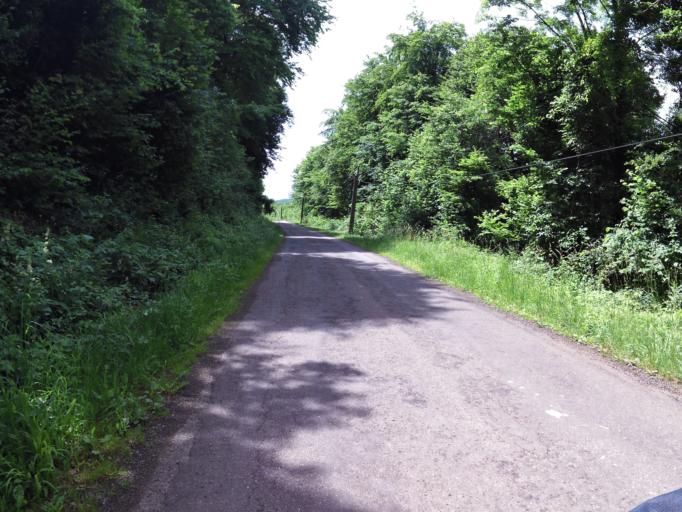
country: FR
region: Lorraine
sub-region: Departement de la Meuse
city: Stenay
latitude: 49.5331
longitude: 5.1147
